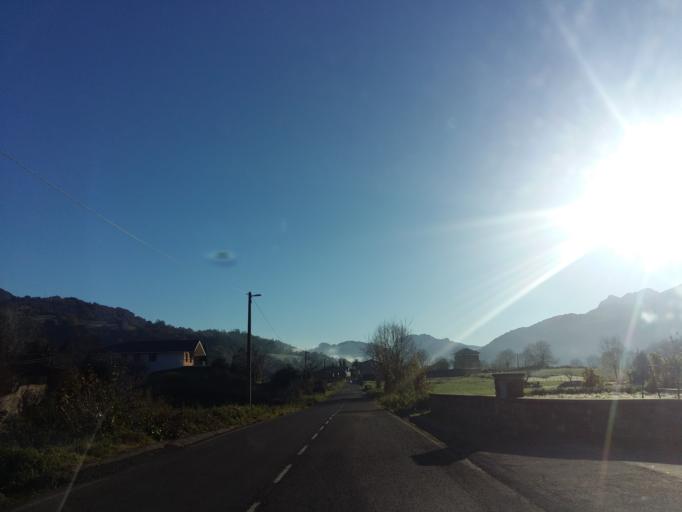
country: ES
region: Cantabria
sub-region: Provincia de Cantabria
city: Arredondo
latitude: 43.2804
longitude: -3.5322
